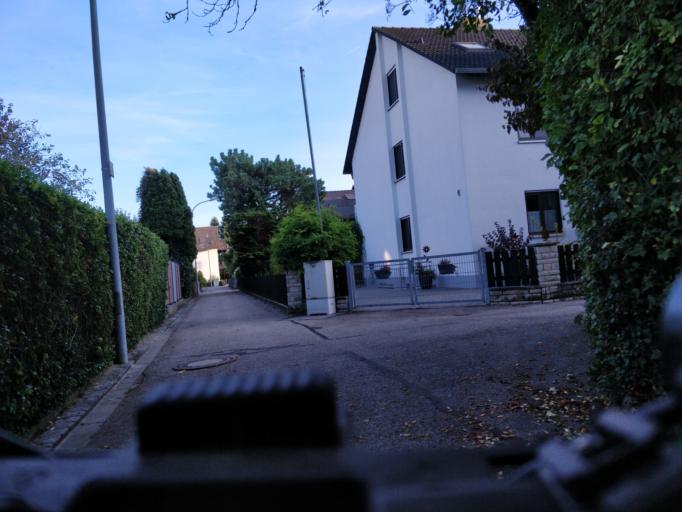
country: DE
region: Bavaria
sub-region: Swabia
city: Mering
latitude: 48.2795
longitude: 10.9722
